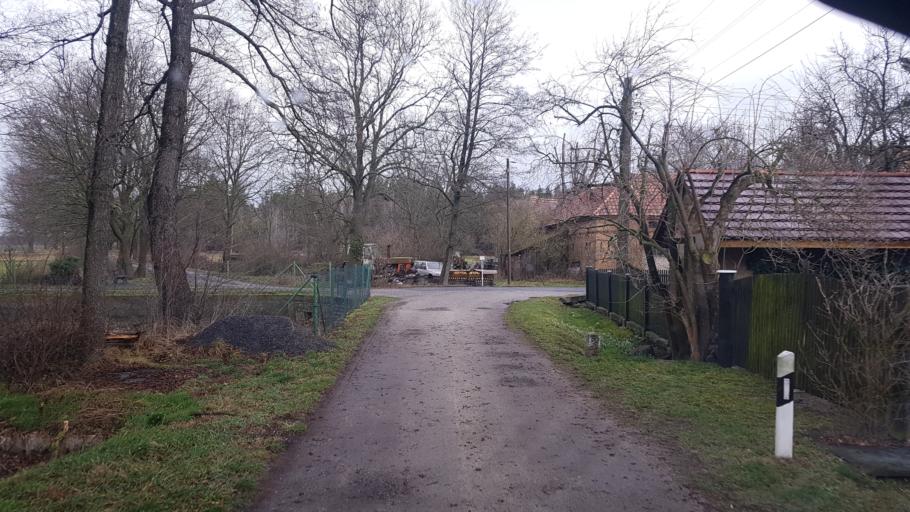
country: DE
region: Brandenburg
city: Sallgast
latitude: 51.6087
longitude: 13.8411
